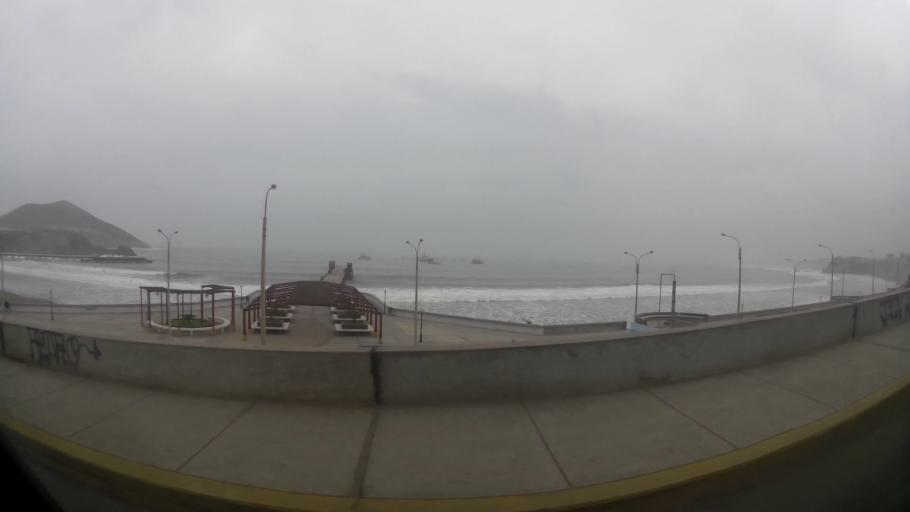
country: PE
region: Lima
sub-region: Provincia de Huaral
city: Chancay
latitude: -11.5838
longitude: -77.2707
